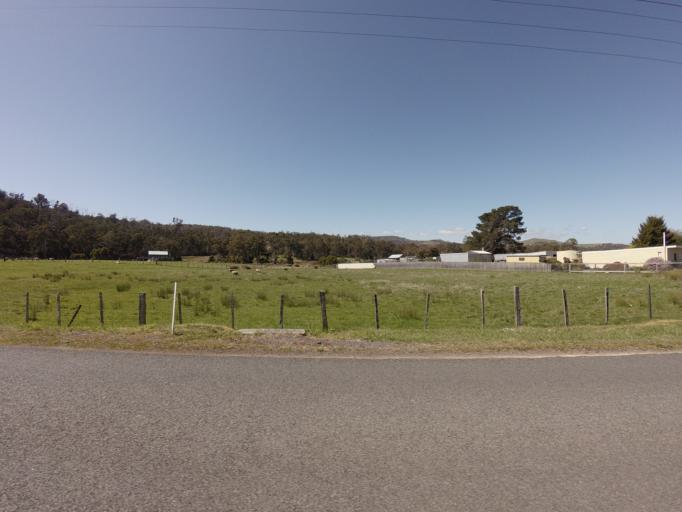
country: AU
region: Tasmania
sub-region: Derwent Valley
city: New Norfolk
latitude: -42.6670
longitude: 146.7888
